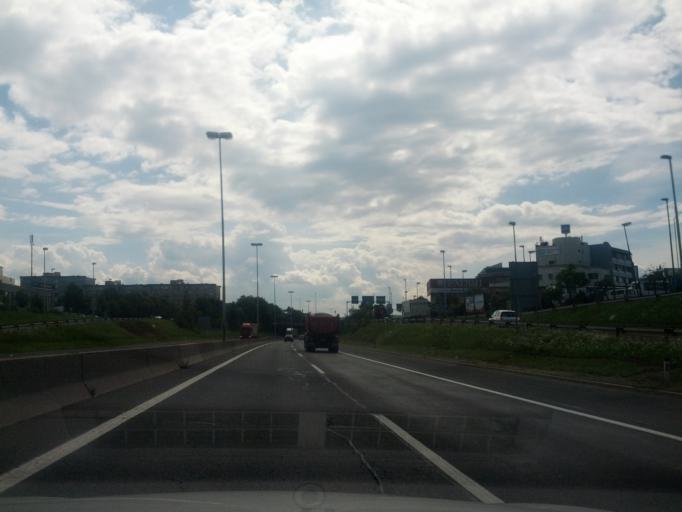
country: SI
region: Ljubljana
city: Ljubljana
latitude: 46.0805
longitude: 14.4846
